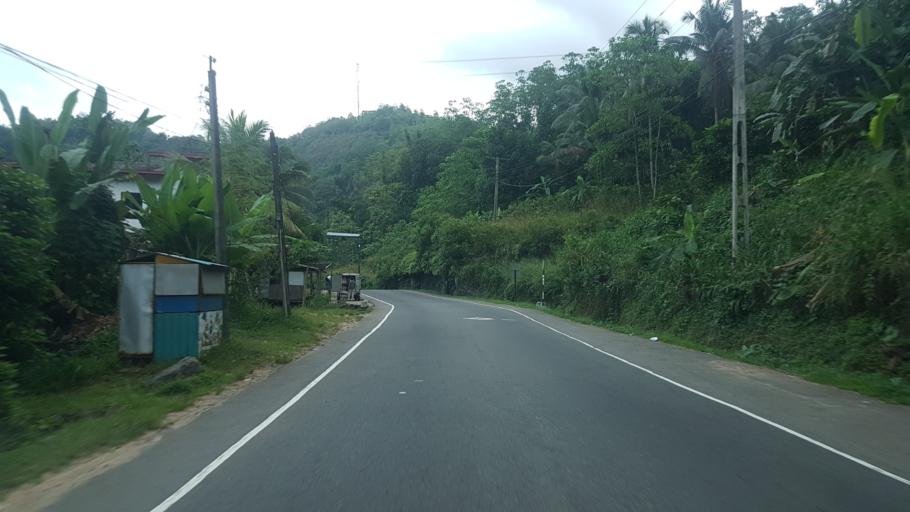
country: LK
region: Western
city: Hanwella Ihala
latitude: 7.0343
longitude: 80.2895
